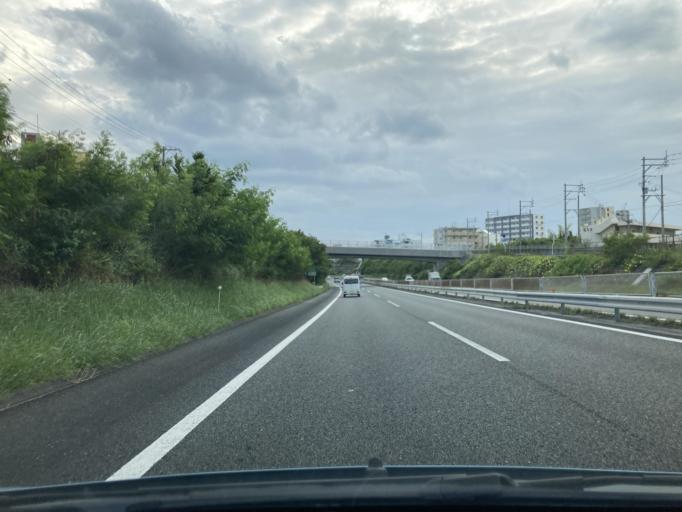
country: JP
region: Okinawa
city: Ginowan
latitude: 26.2572
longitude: 127.7662
